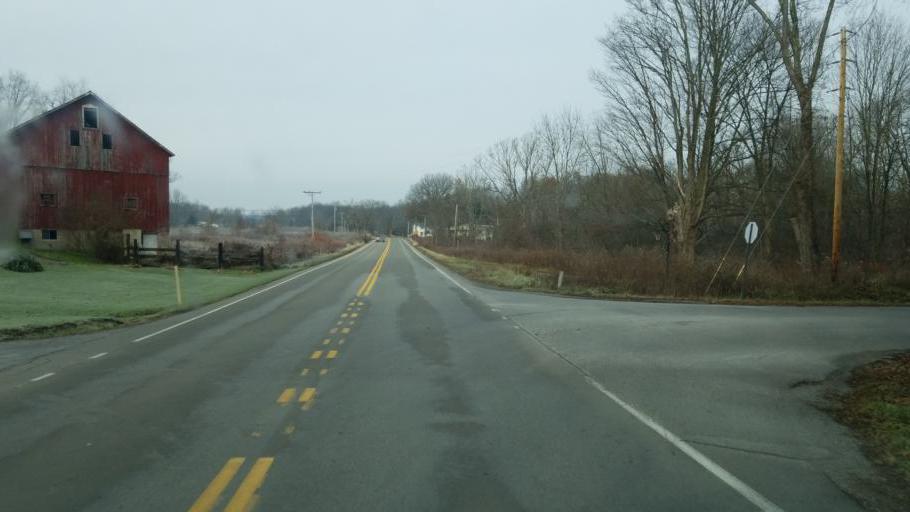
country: US
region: Pennsylvania
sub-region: Crawford County
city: Meadville
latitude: 41.5312
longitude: -80.1593
